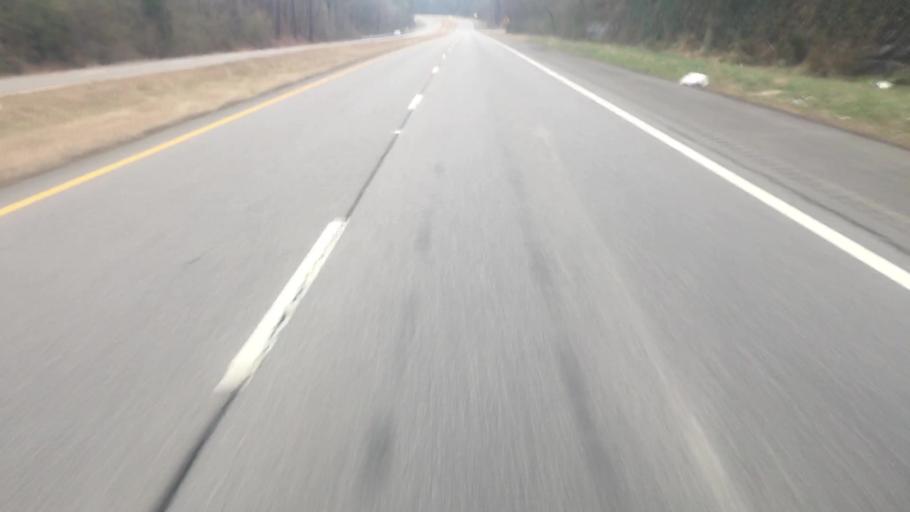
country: US
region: Alabama
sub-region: Walker County
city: Cordova
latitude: 33.8239
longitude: -87.1930
